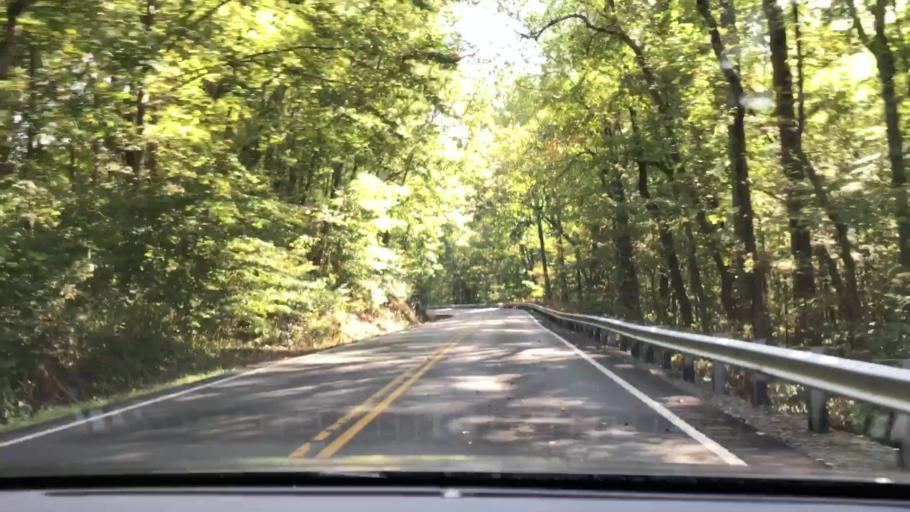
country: US
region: Kentucky
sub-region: Marshall County
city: Benton
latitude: 36.7661
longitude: -88.2713
